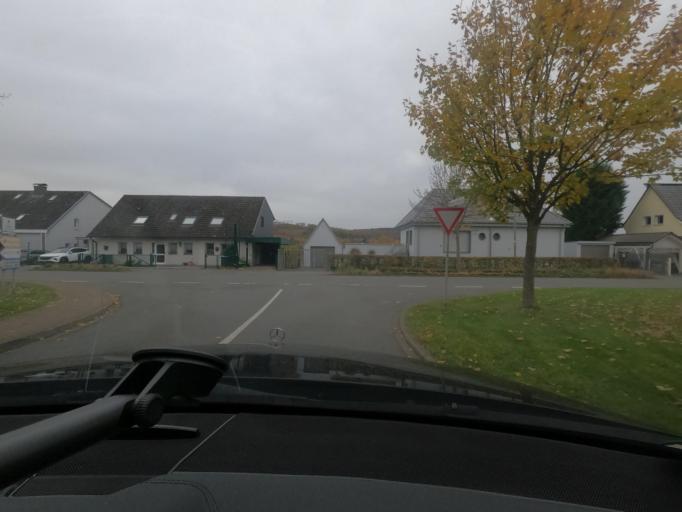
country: DE
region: North Rhine-Westphalia
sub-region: Regierungsbezirk Arnsberg
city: Mohnesee
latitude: 51.4873
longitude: 8.1727
